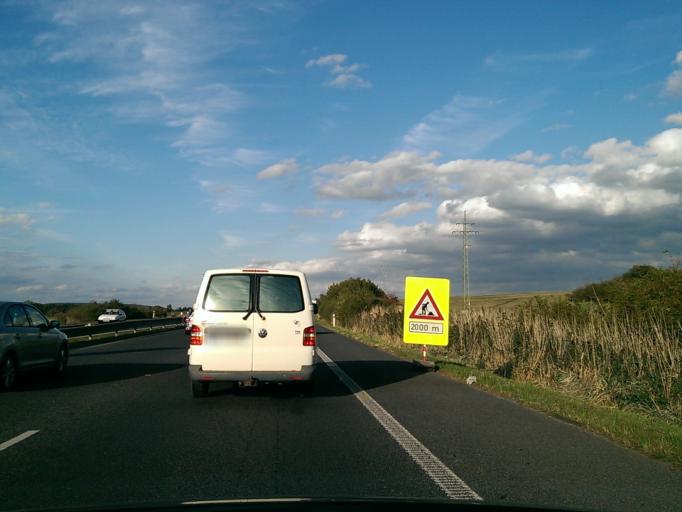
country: CZ
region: Central Bohemia
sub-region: Okres Mlada Boleslav
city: Mlada Boleslav
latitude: 50.3954
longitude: 14.9107
